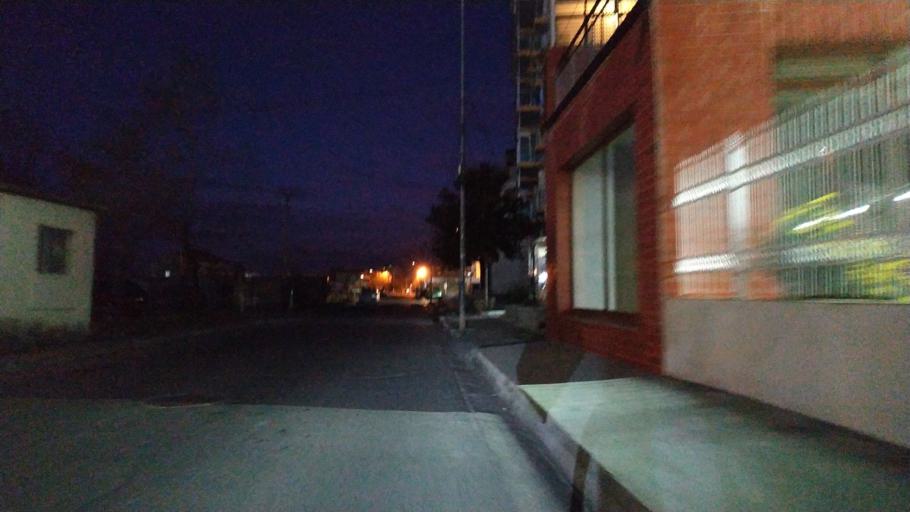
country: AL
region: Shkoder
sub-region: Rrethi i Shkodres
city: Shkoder
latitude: 42.0561
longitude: 19.4995
